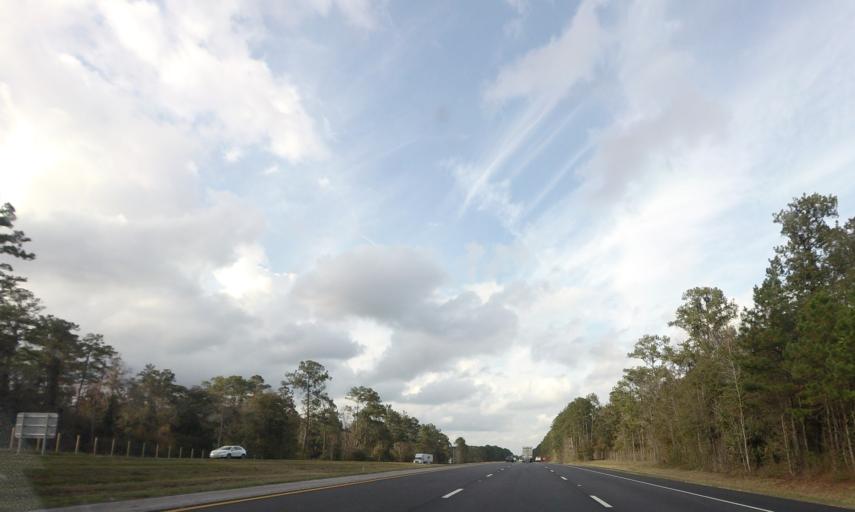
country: US
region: Florida
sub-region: Alachua County
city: Alachua
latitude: 29.7049
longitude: -82.4596
